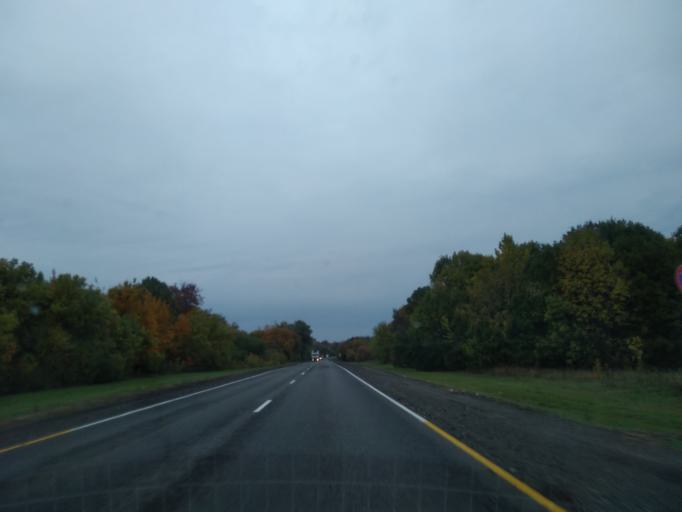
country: RU
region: Lipetsk
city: Zadonsk
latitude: 52.4868
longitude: 38.7597
